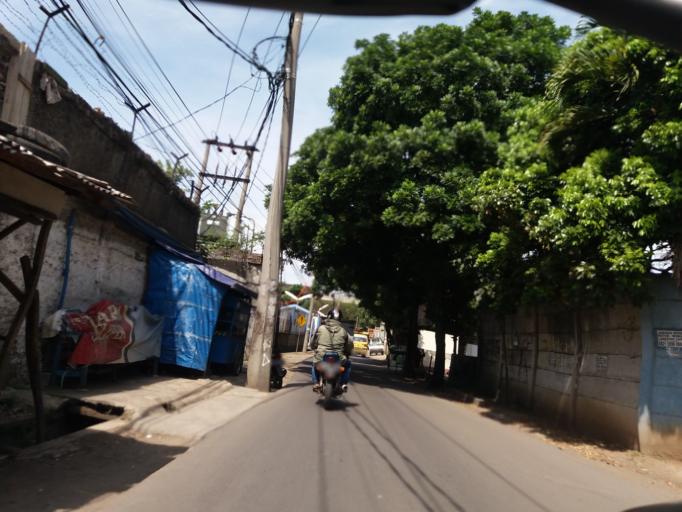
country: ID
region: West Java
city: Margahayukencana
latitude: -6.9427
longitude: 107.5675
